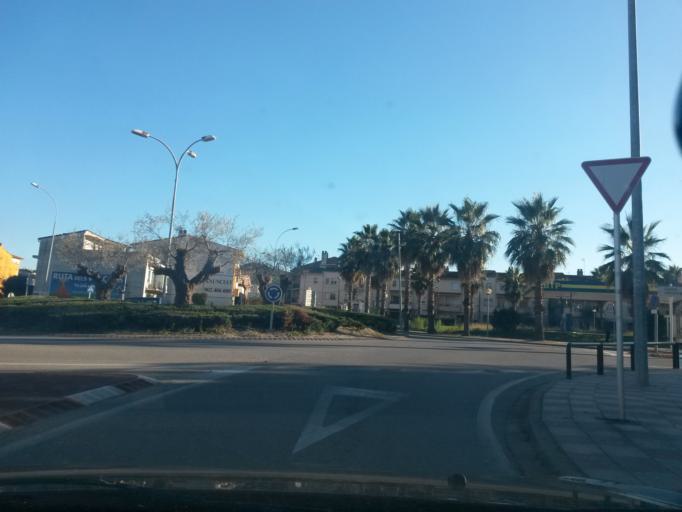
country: ES
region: Catalonia
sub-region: Provincia de Girona
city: Angles
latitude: 41.9587
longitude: 2.6344
